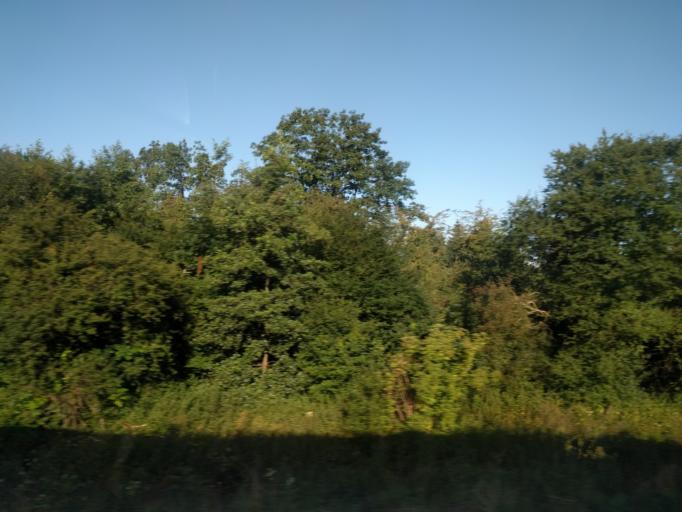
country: DK
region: Zealand
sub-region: Roskilde Kommune
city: Svogerslev
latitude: 55.6050
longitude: 12.0457
